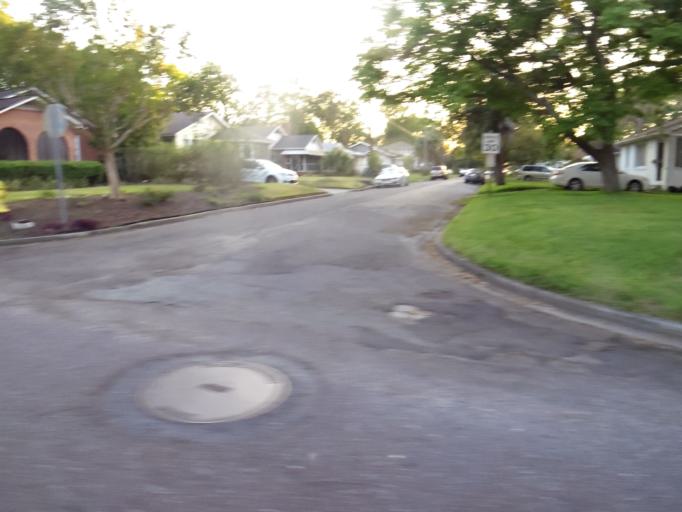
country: US
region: Florida
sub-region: Duval County
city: Jacksonville
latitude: 30.3107
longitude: -81.7033
